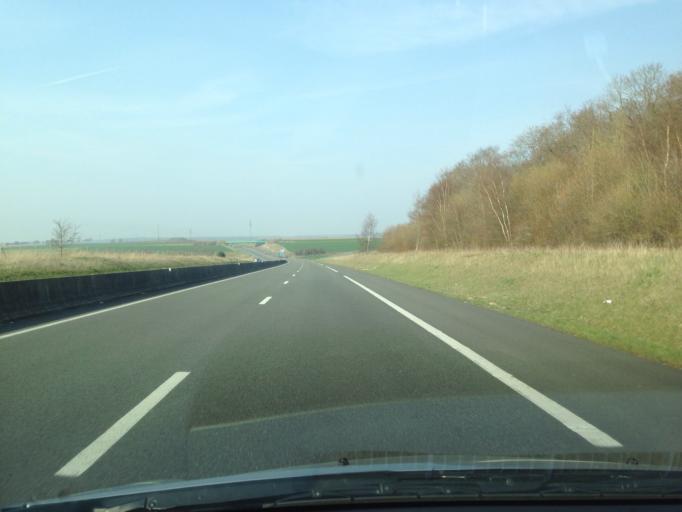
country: FR
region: Picardie
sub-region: Departement de la Somme
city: Sailly-Flibeaucourt
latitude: 50.1880
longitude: 1.7561
